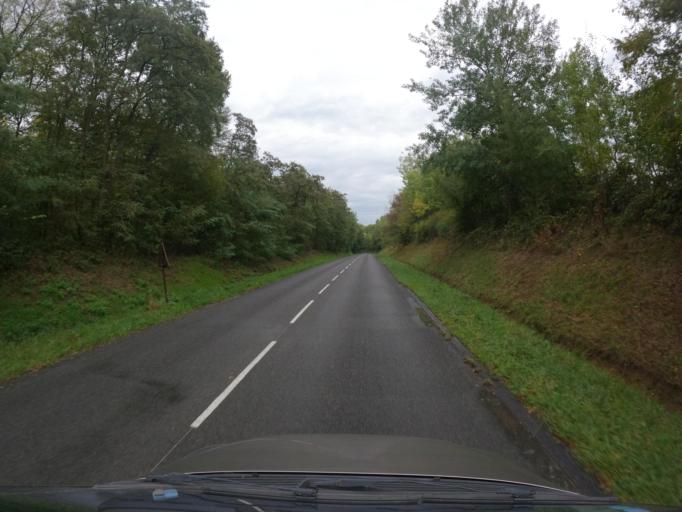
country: FR
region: Ile-de-France
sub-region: Departement de Seine-et-Marne
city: Serris
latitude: 48.8263
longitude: 2.7666
